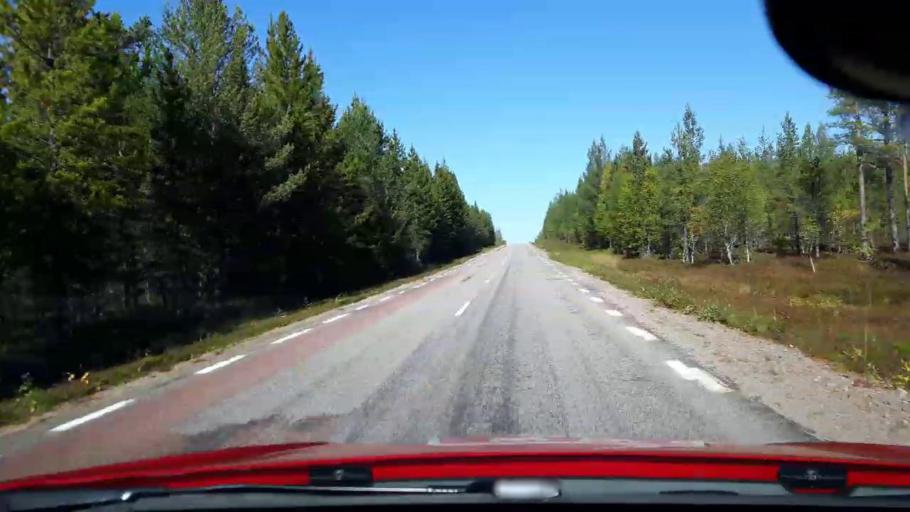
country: SE
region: Jaemtland
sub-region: Harjedalens Kommun
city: Sveg
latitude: 61.7262
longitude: 14.1663
